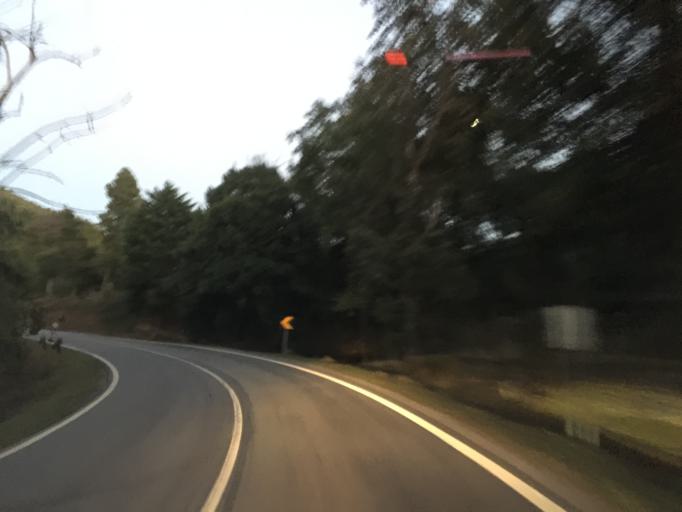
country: PT
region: Portalegre
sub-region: Castelo de Vide
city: Castelo de Vide
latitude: 39.4007
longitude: -7.4325
